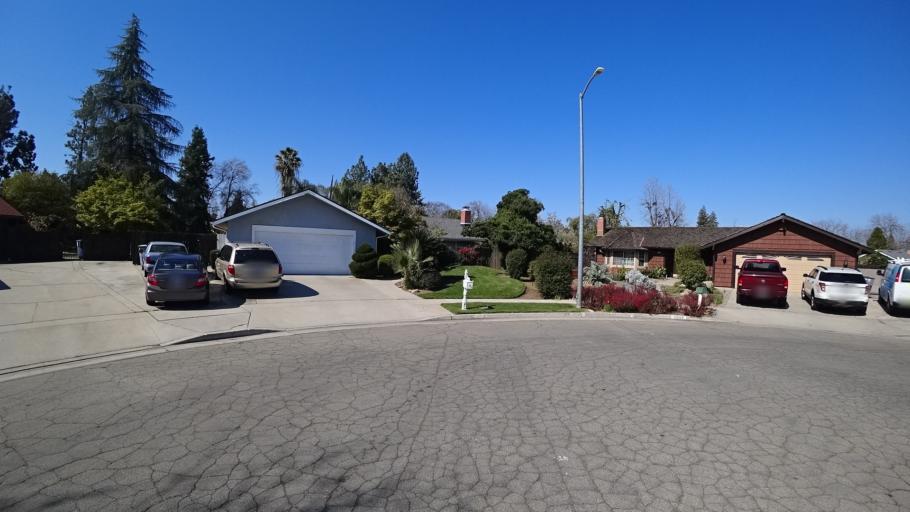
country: US
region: California
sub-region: Fresno County
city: Clovis
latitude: 36.8327
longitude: -119.7311
